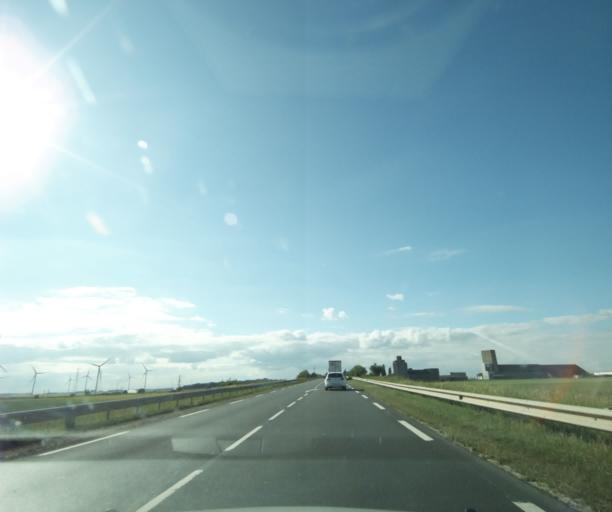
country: FR
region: Centre
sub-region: Departement d'Eure-et-Loir
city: Voves
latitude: 48.3191
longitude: 1.6720
